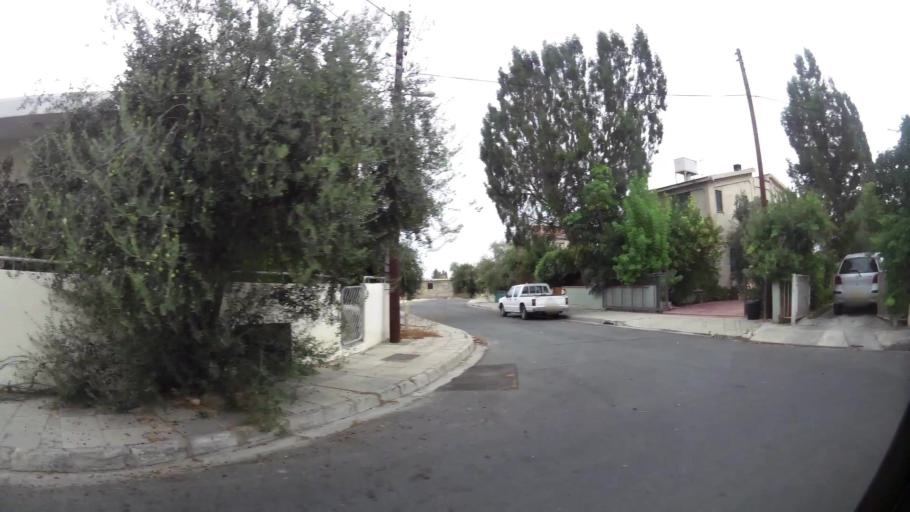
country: CY
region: Lefkosia
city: Geri
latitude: 35.1094
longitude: 33.3850
